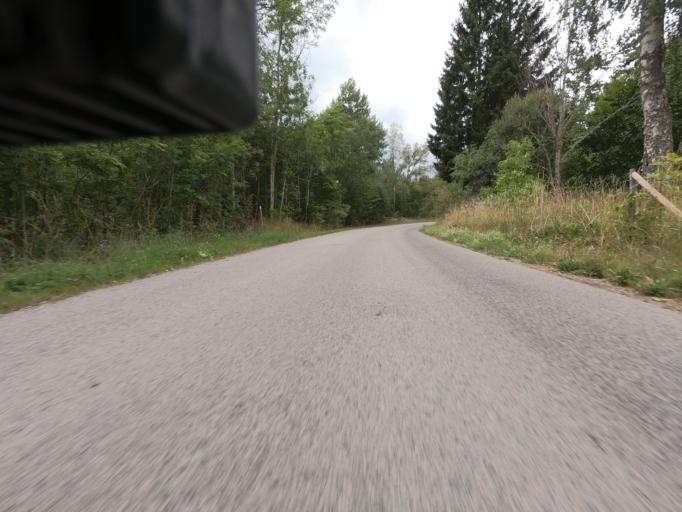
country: SE
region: Kronoberg
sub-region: Vaxjo Kommun
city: Rottne
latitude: 57.0832
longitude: 14.9452
